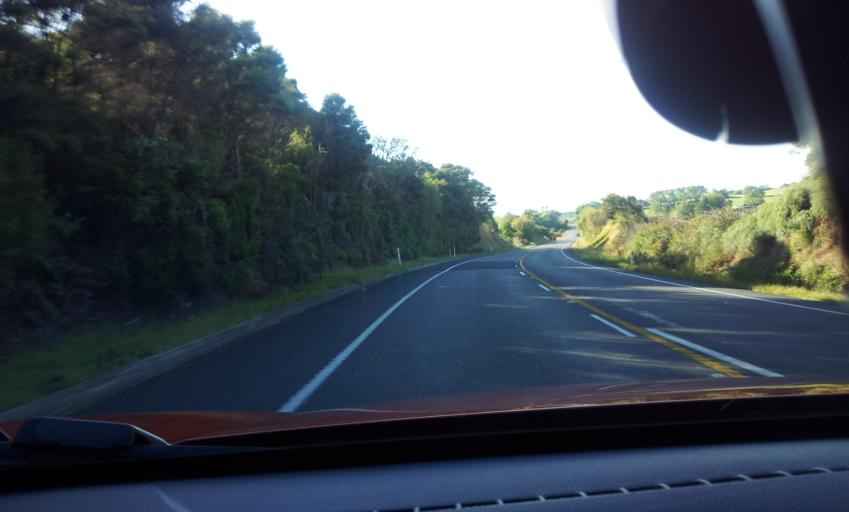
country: NZ
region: Waikato
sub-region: Hauraki District
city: Ngatea
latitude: -37.3142
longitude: 175.3941
